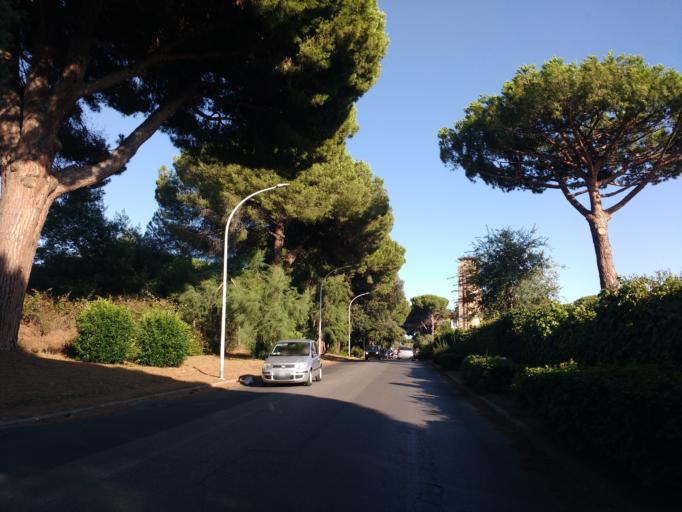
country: IT
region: Latium
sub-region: Citta metropolitana di Roma Capitale
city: Acilia-Castel Fusano-Ostia Antica
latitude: 41.7607
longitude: 12.3620
